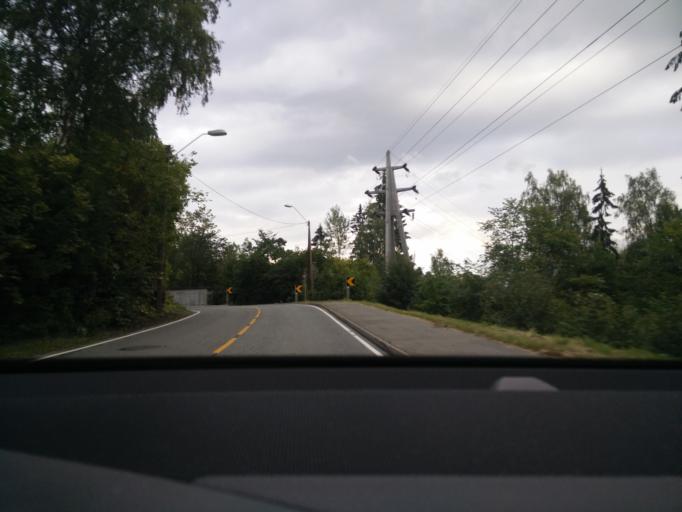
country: NO
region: Akershus
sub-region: Baerum
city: Lysaker
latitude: 59.9256
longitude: 10.6251
